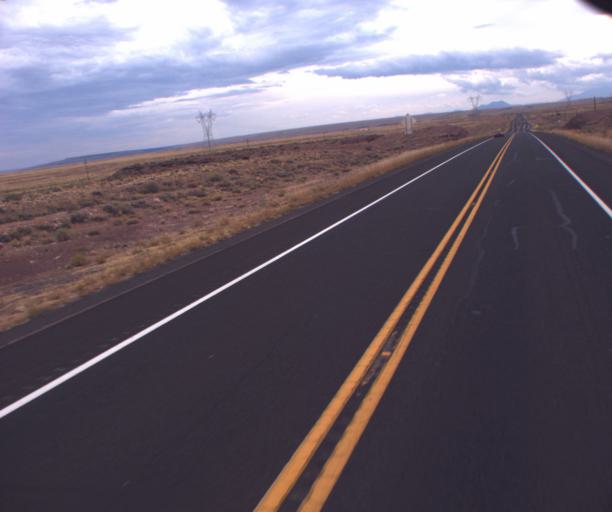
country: US
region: Arizona
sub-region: Coconino County
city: Tuba City
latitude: 35.8291
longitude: -111.4386
